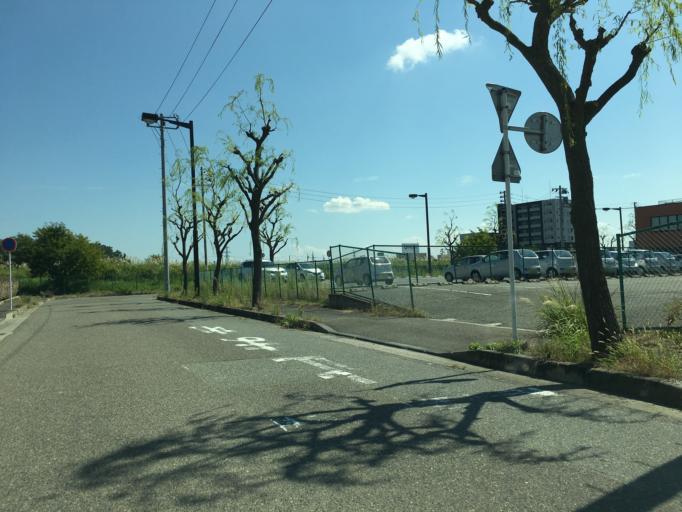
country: JP
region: Niigata
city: Niigata-shi
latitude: 37.8946
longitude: 139.0171
